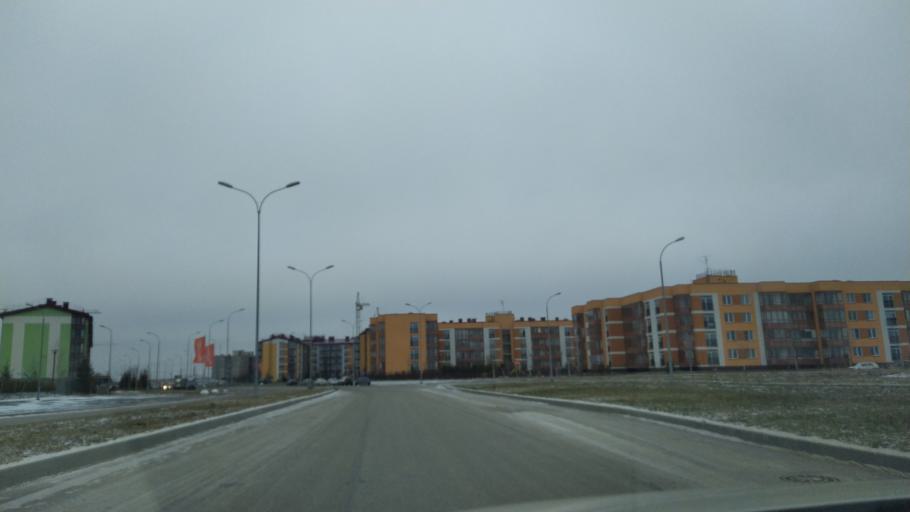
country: RU
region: St.-Petersburg
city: Aleksandrovskaya
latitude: 59.7541
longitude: 30.3641
